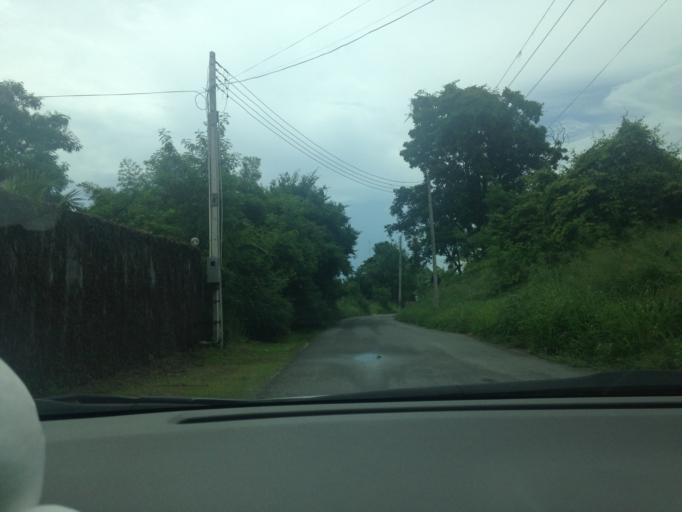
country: TH
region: Chon Buri
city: Chon Buri
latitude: 13.3293
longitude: 100.9259
